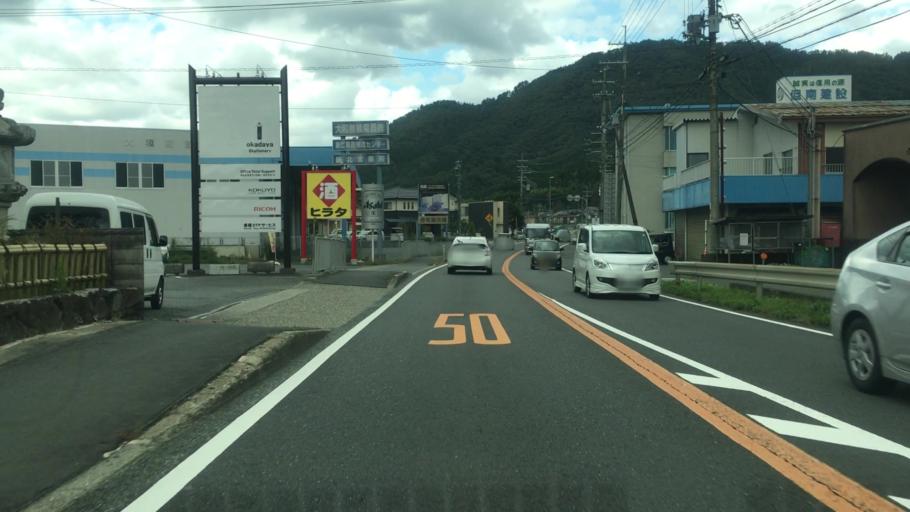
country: JP
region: Hyogo
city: Toyooka
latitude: 35.3221
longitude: 134.8785
